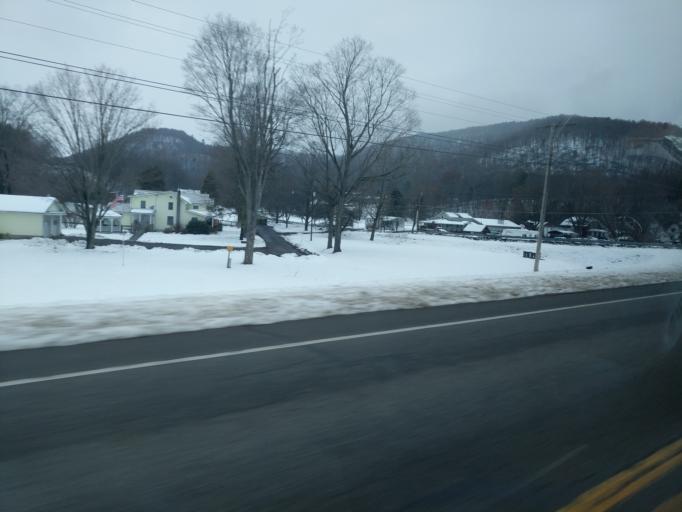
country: US
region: Pennsylvania
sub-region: Tioga County
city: Wellsboro
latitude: 41.8564
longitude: -77.2377
